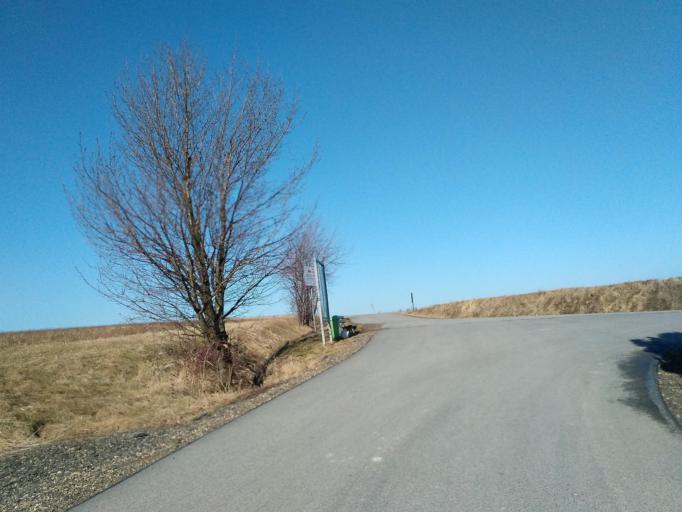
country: PL
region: Subcarpathian Voivodeship
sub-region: Powiat rzeszowski
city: Lubenia
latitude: 49.9355
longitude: 21.9437
